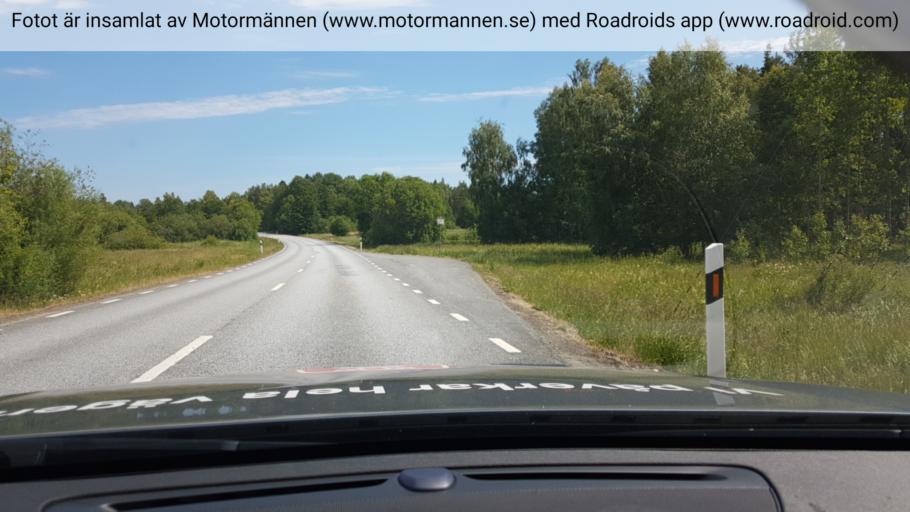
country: SE
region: Uppsala
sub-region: Osthammars Kommun
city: Marieberg
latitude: 60.1657
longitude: 18.4541
